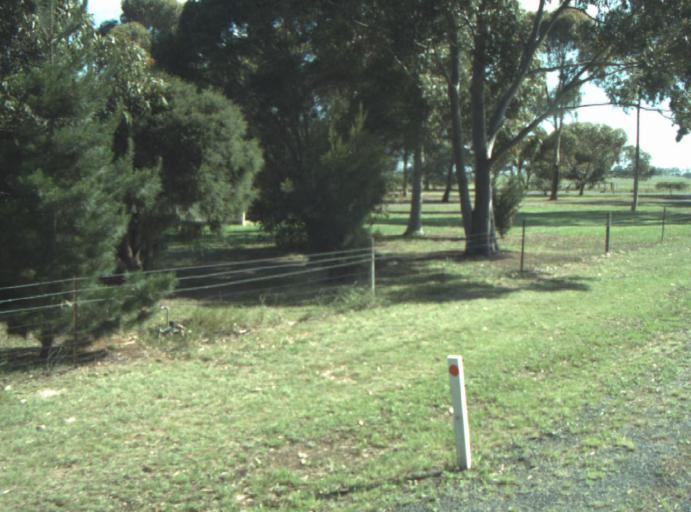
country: AU
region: Victoria
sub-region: Greater Geelong
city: Lara
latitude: -37.9998
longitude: 144.4427
